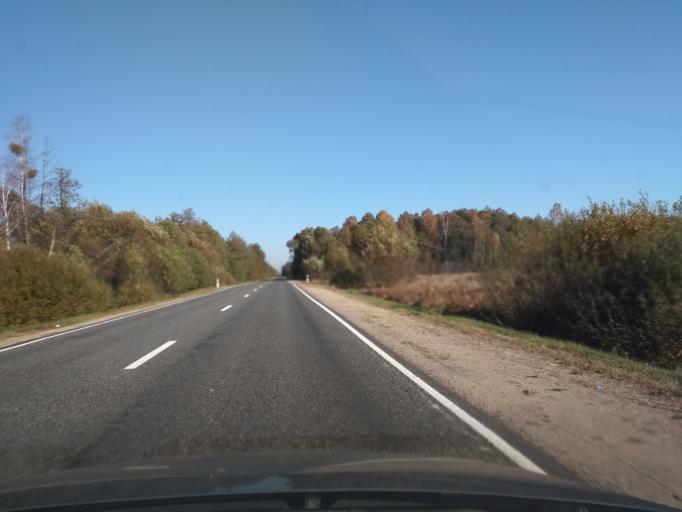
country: BY
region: Brest
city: Malaryta
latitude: 51.8970
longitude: 24.1419
